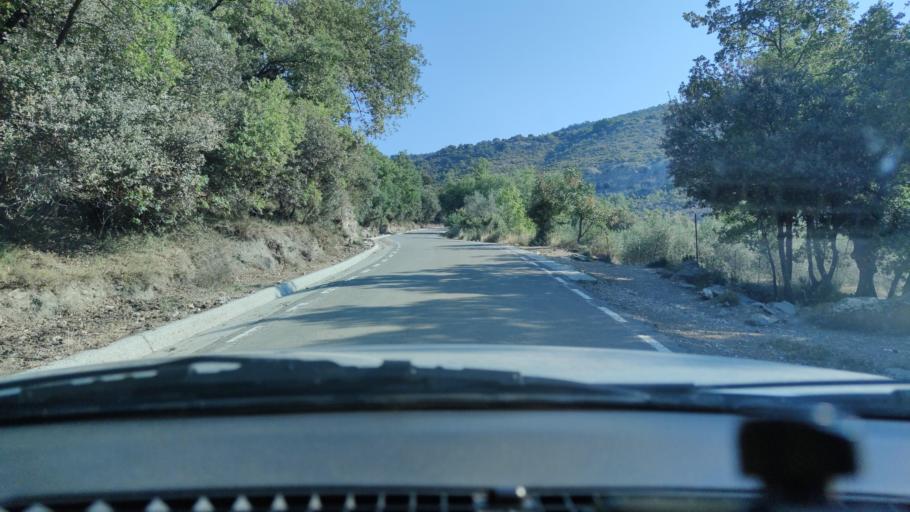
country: ES
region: Catalonia
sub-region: Provincia de Lleida
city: Llimiana
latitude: 42.0838
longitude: 0.8421
